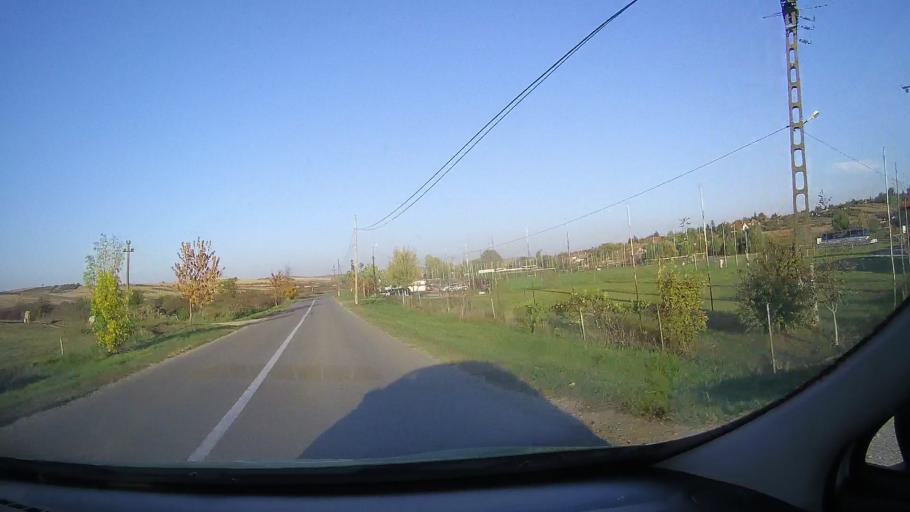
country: RO
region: Bihor
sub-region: Comuna Paleu
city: Paleu
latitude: 47.1187
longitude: 21.9509
